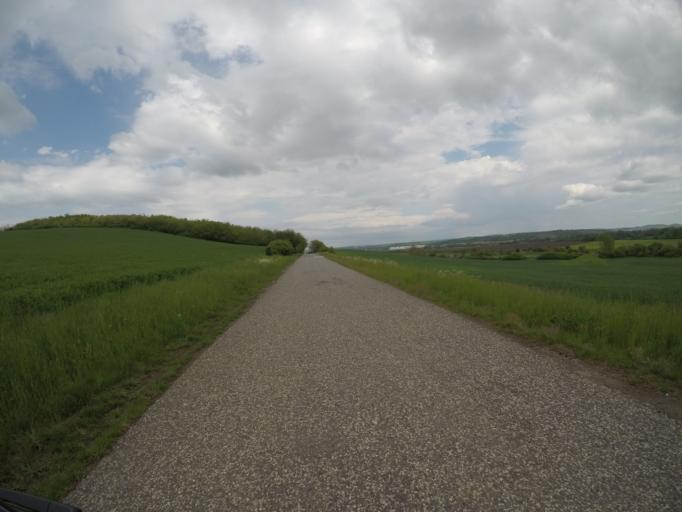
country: SK
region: Nitriansky
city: Sahy
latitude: 48.0835
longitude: 18.8666
